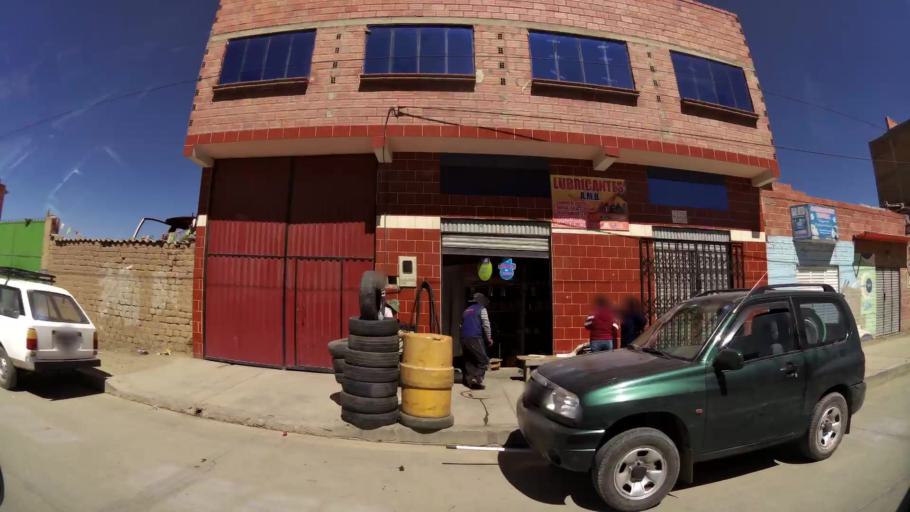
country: BO
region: La Paz
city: La Paz
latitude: -16.5090
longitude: -68.2149
